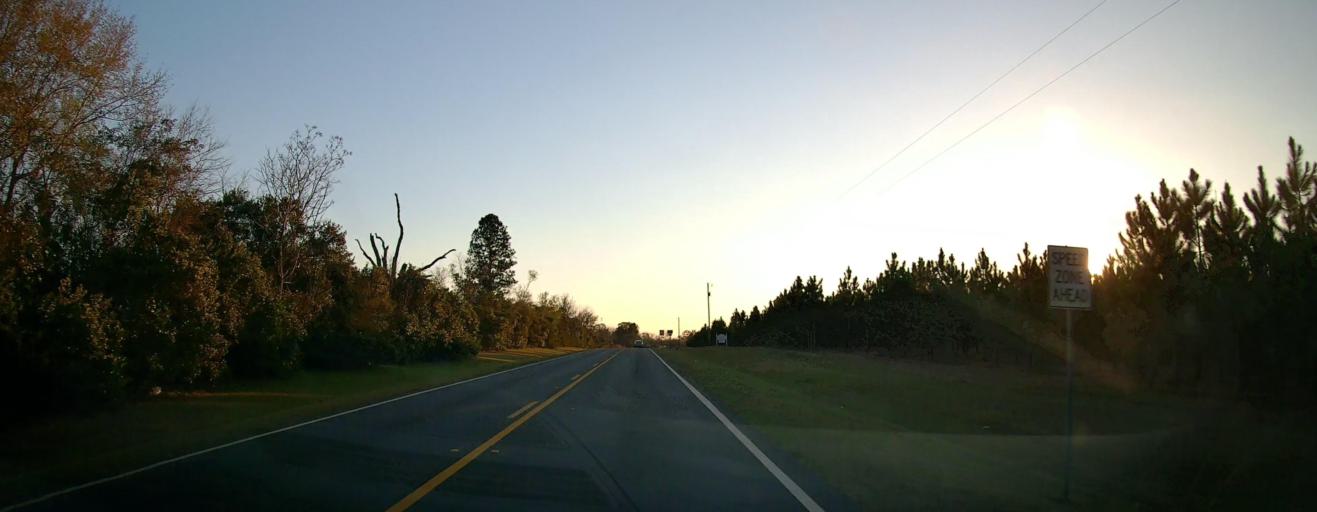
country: US
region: Georgia
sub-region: Laurens County
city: Dublin
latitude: 32.3918
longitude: -82.9827
